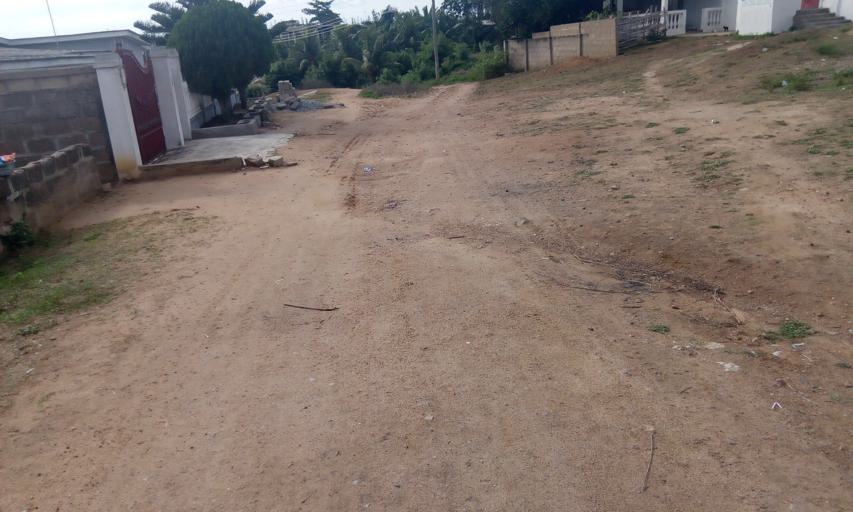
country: GH
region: Central
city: Winneba
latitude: 5.3595
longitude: -0.6240
